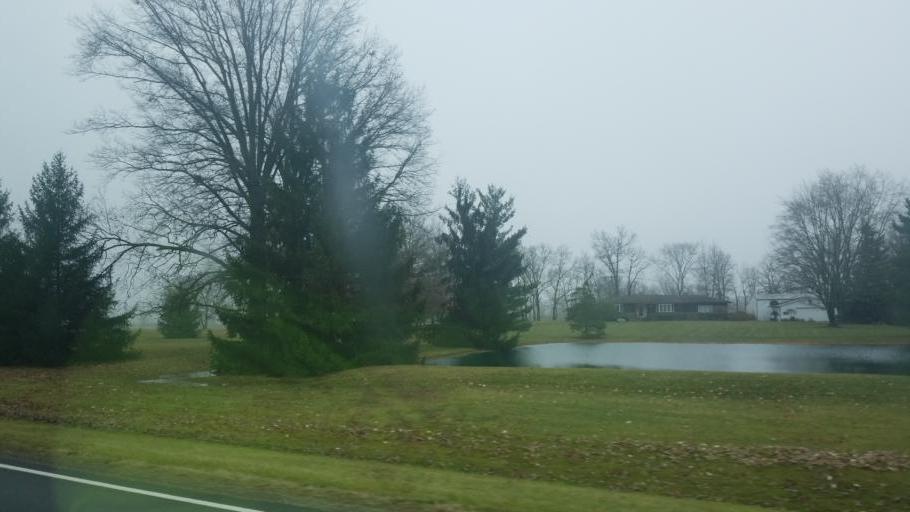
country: US
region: Ohio
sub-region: Union County
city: Marysville
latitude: 40.2576
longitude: -83.4487
